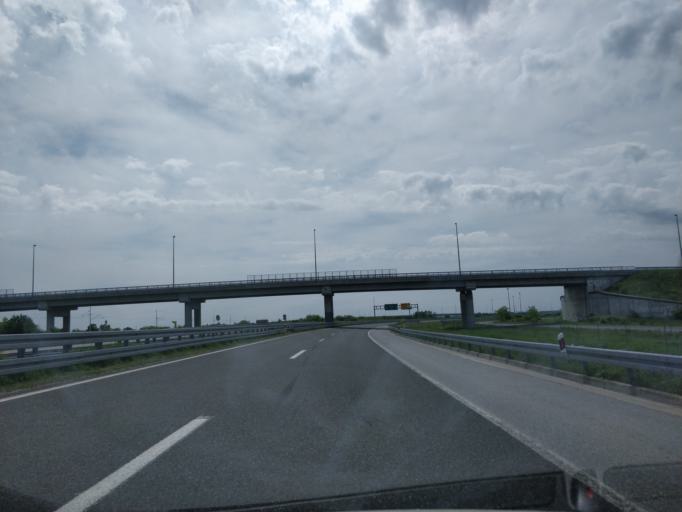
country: HR
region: Zagrebacka
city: Gradici
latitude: 45.6988
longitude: 16.0592
